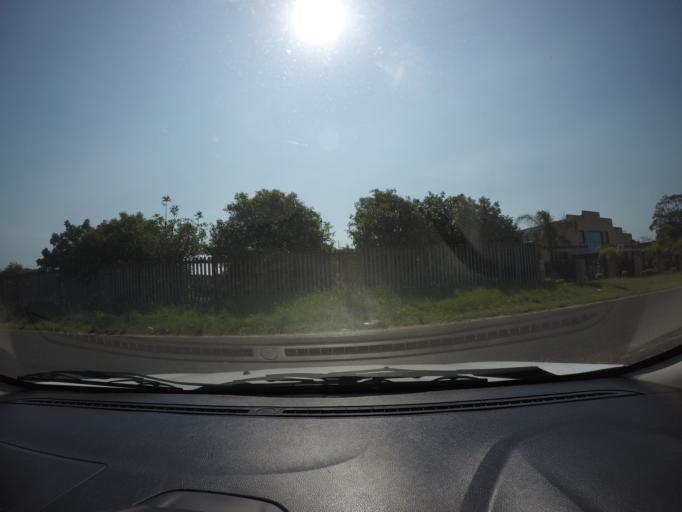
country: ZA
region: KwaZulu-Natal
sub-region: uThungulu District Municipality
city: Richards Bay
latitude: -28.7225
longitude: 32.0436
